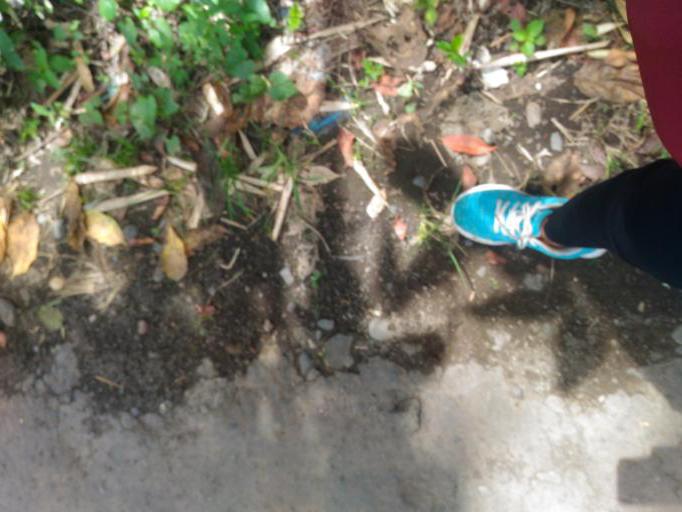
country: ID
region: East Java
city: Sumbersewu
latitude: -8.4099
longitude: 114.3182
